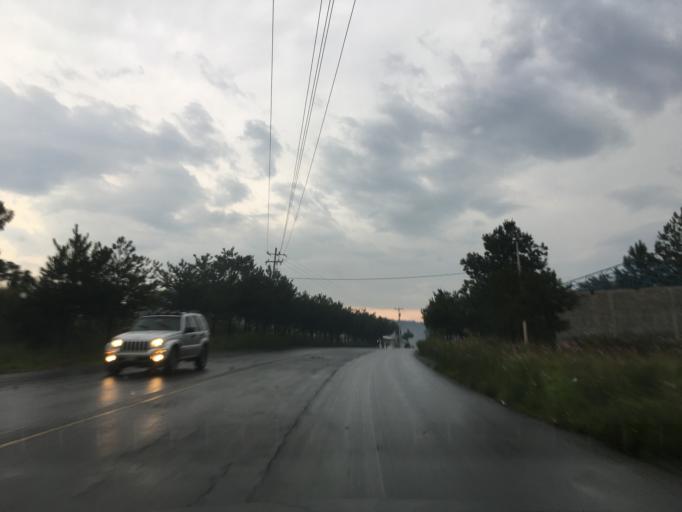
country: MX
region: Michoacan
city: Capacuaro
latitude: 19.5301
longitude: -102.0968
